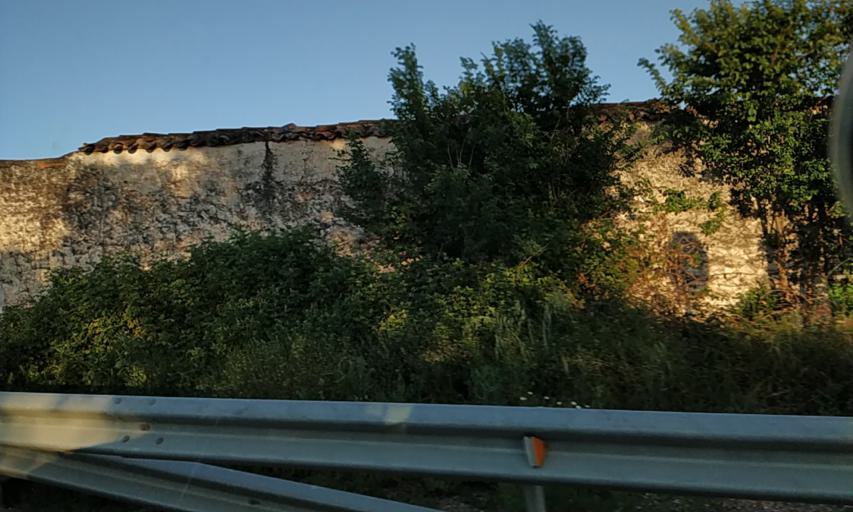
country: ES
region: Extremadura
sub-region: Provincia de Caceres
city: Valencia de Alcantara
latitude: 39.4273
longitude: -7.2253
